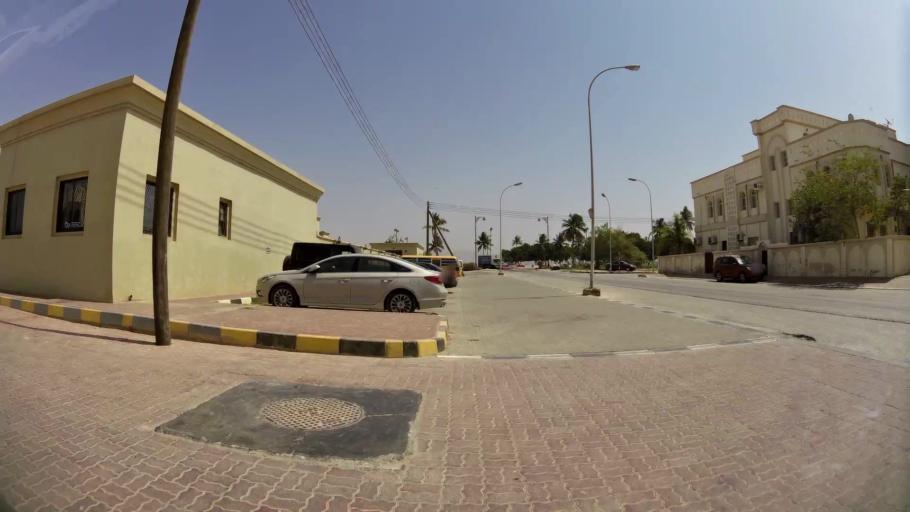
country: OM
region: Zufar
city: Salalah
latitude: 17.0221
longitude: 54.1046
